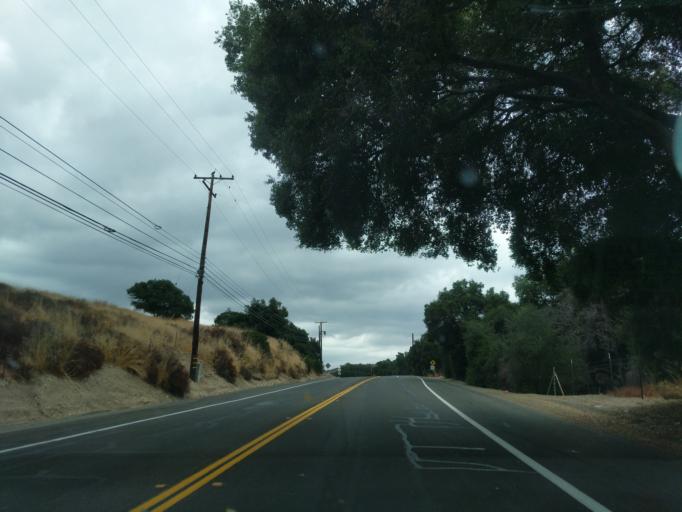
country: US
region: California
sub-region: Orange County
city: Foothill Ranch
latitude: 33.7590
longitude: -117.7012
